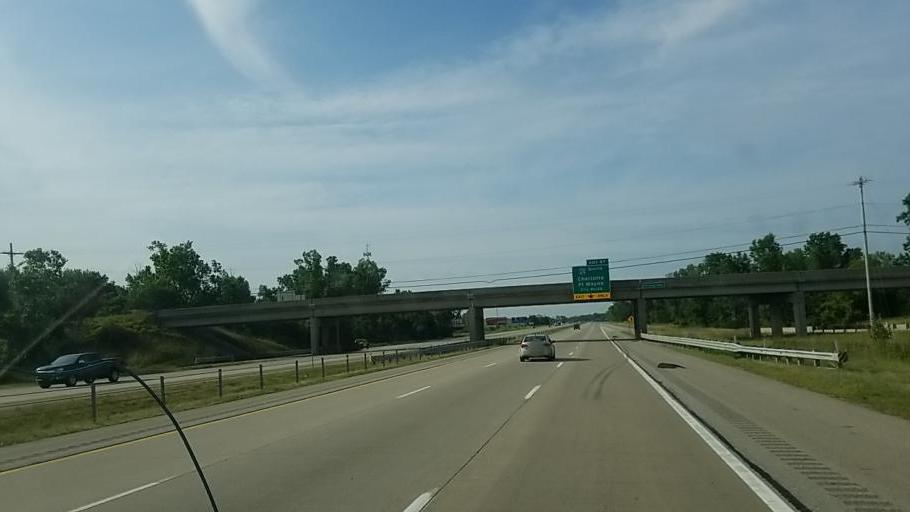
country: US
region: Michigan
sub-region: Eaton County
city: Waverly
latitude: 42.7131
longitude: -84.6695
